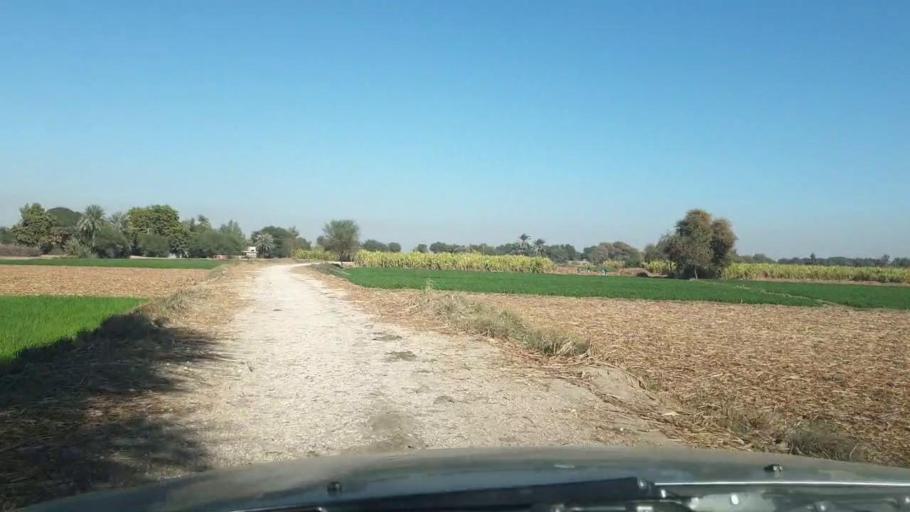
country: PK
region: Sindh
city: Ghotki
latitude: 28.0532
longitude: 69.2445
